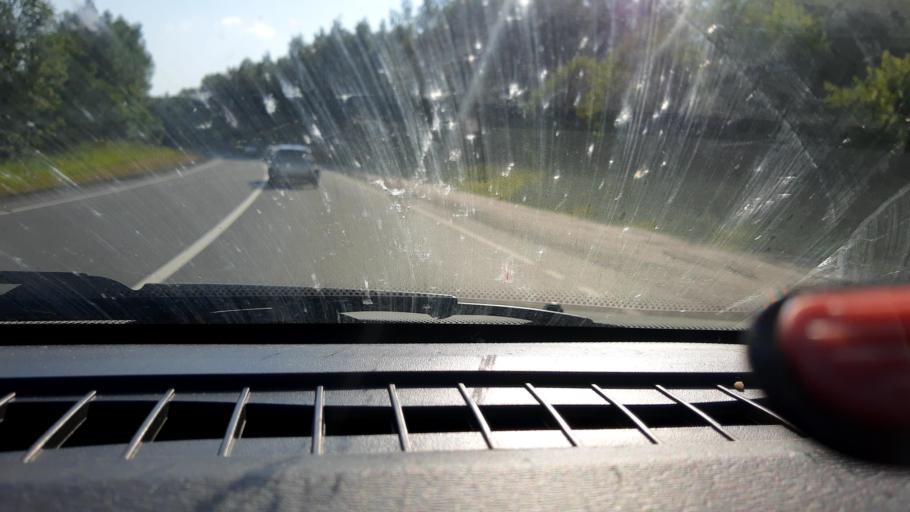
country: RU
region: Nizjnij Novgorod
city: Linda
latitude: 56.7064
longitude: 44.2248
